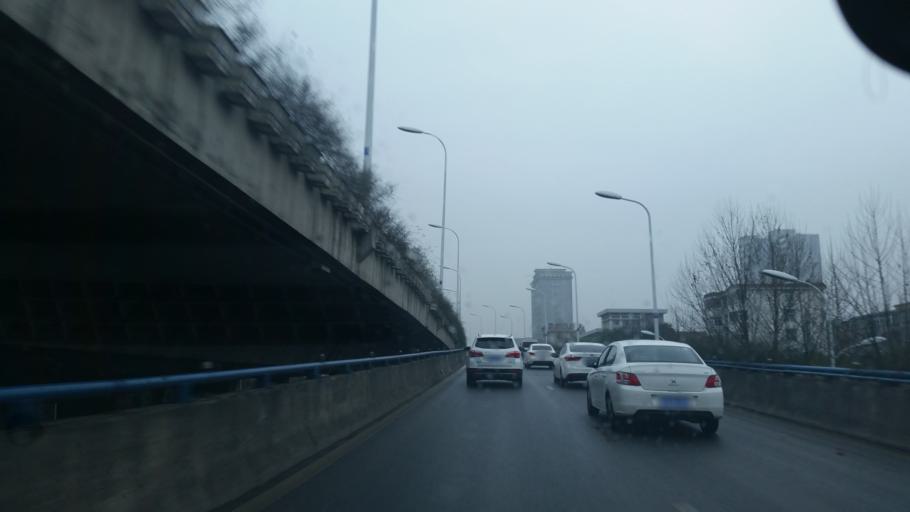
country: CN
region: Anhui Sheng
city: Hefei
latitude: 31.8588
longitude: 117.2075
